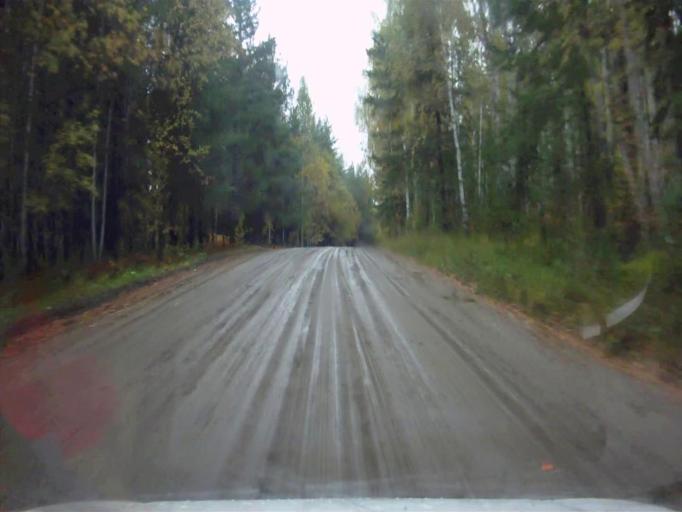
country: RU
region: Chelyabinsk
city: Kyshtym
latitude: 55.8866
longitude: 60.4652
